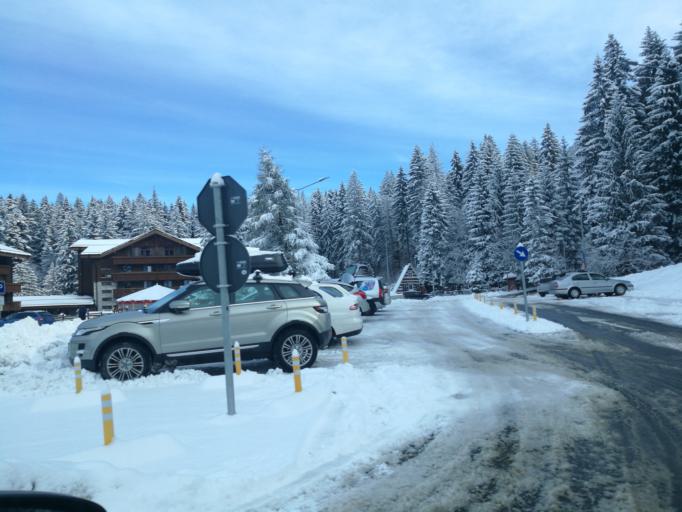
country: RO
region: Brasov
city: Brasov
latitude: 45.5883
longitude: 25.5521
